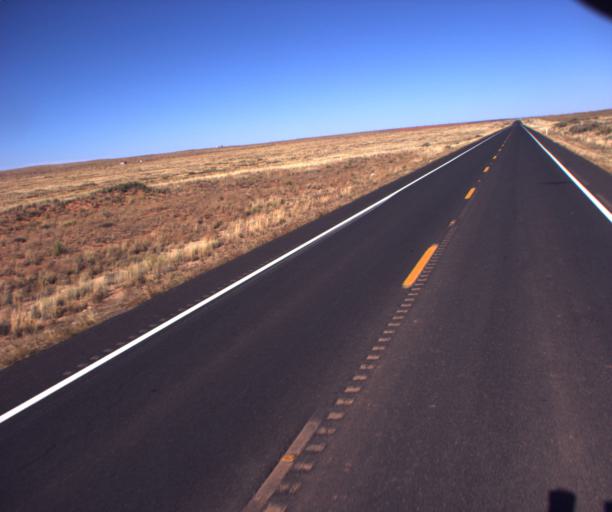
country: US
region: Arizona
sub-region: Coconino County
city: Kaibito
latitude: 36.3670
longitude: -110.8980
